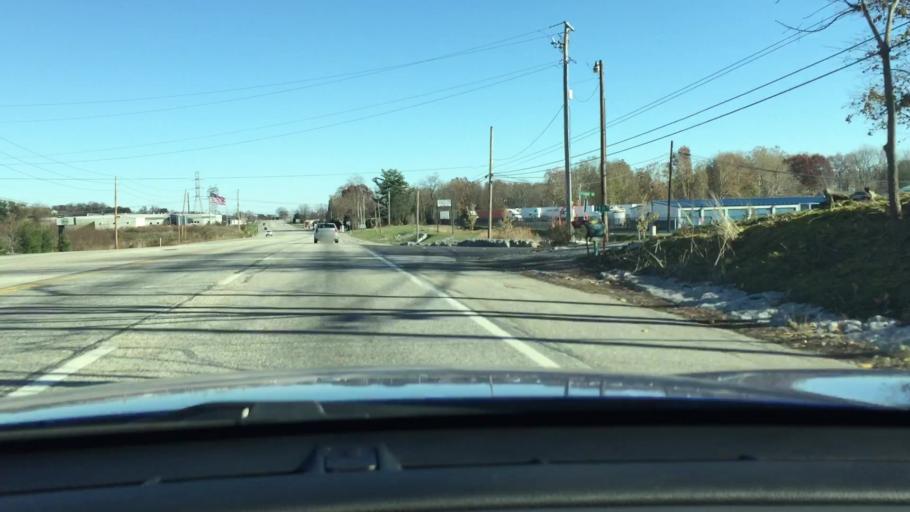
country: US
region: Pennsylvania
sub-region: Cumberland County
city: Schlusser
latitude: 40.2327
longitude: -77.1080
